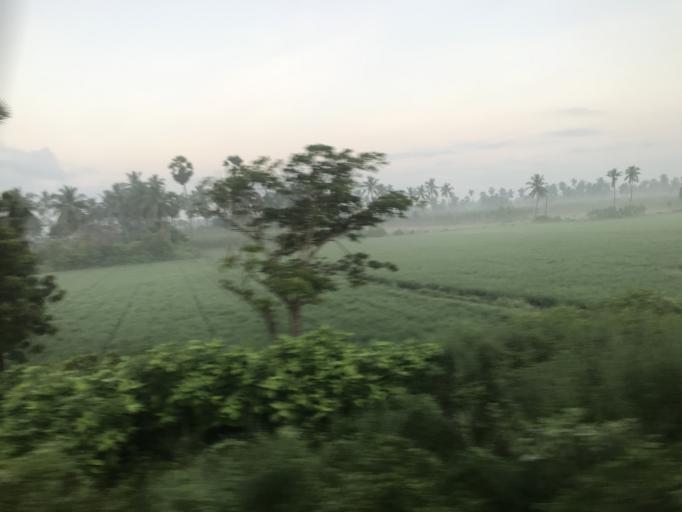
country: IN
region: Andhra Pradesh
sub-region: Guntur
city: Ponnur
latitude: 16.0808
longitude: 80.5633
